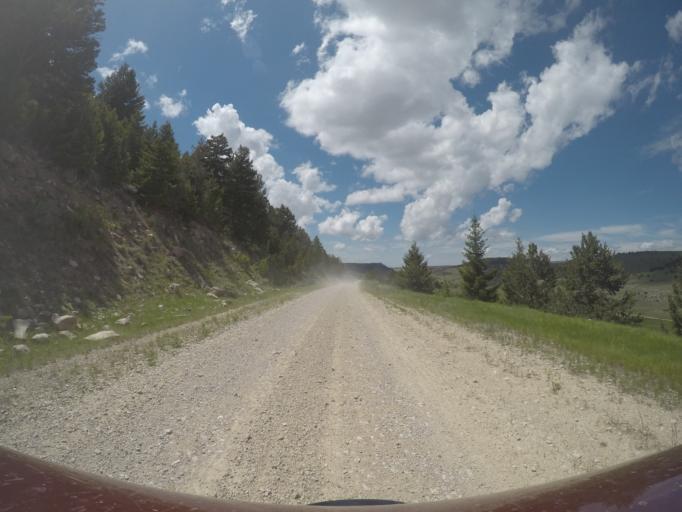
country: US
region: Wyoming
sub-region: Big Horn County
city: Lovell
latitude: 45.2089
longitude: -108.5483
